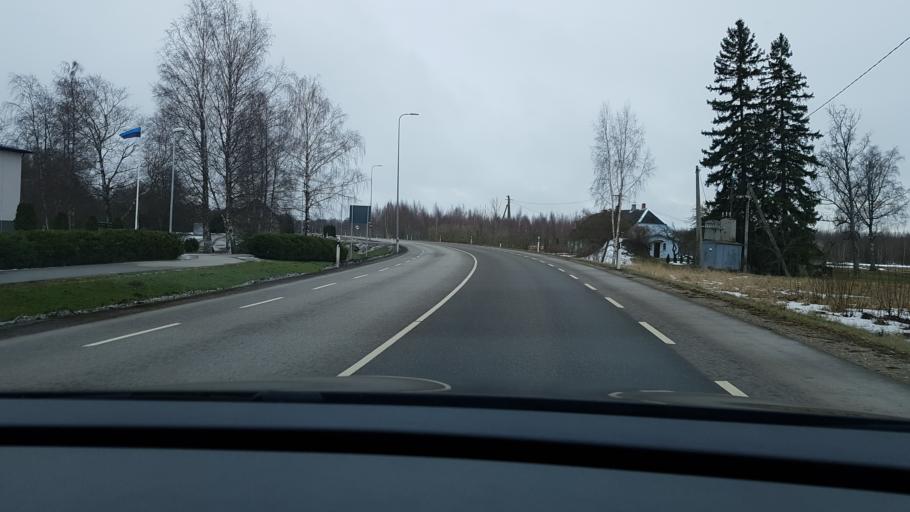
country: EE
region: Paernumaa
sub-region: Sauga vald
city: Sauga
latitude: 58.4304
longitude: 24.4384
